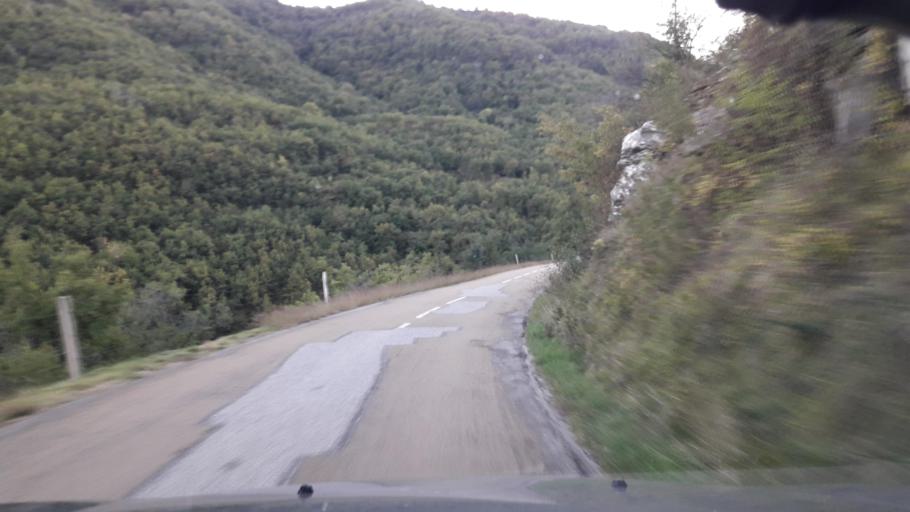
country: FR
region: Rhone-Alpes
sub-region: Departement de l'Ardeche
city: Saint-Priest
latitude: 44.6999
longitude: 4.5625
